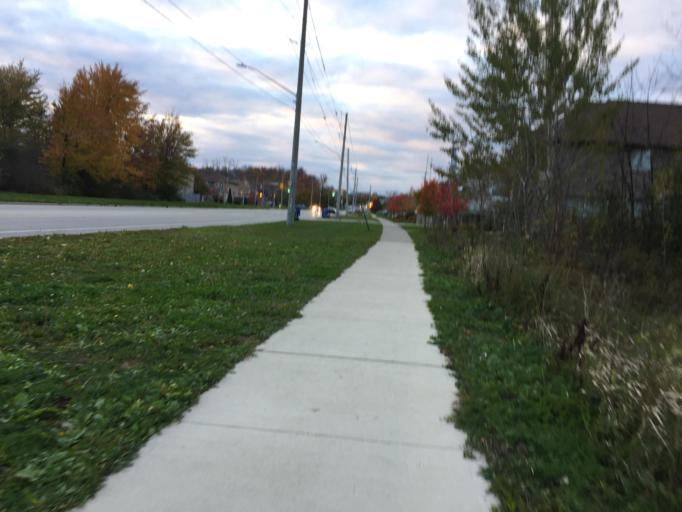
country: CA
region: Ontario
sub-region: Wellington County
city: Guelph
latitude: 43.5258
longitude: -80.2967
